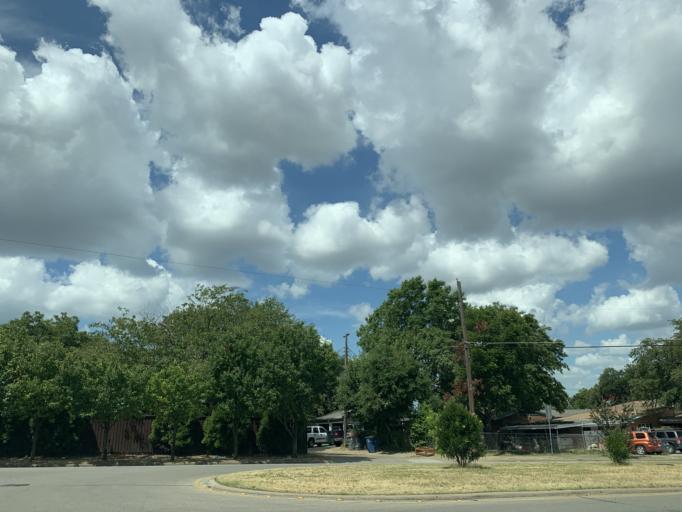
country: US
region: Texas
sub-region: Dallas County
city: Cockrell Hill
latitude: 32.7468
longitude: -96.8622
